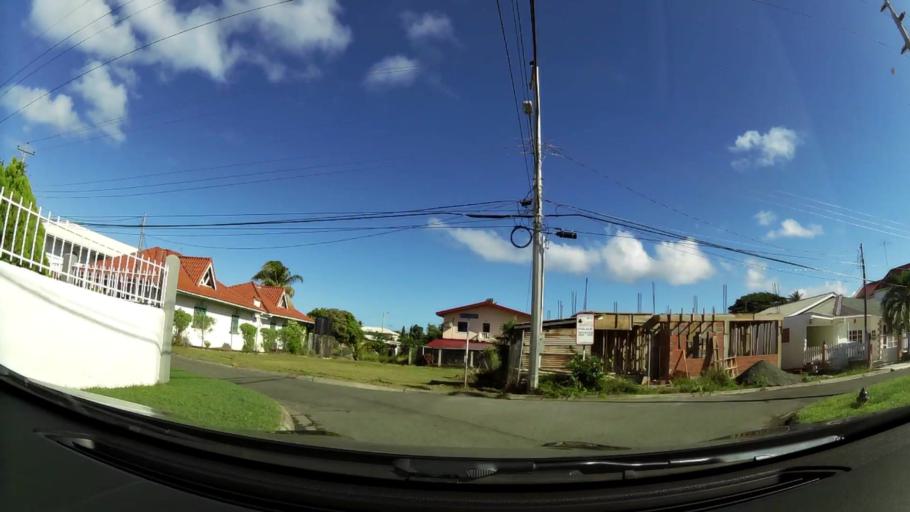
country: TT
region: Tobago
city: Scarborough
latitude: 11.1589
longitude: -60.8335
